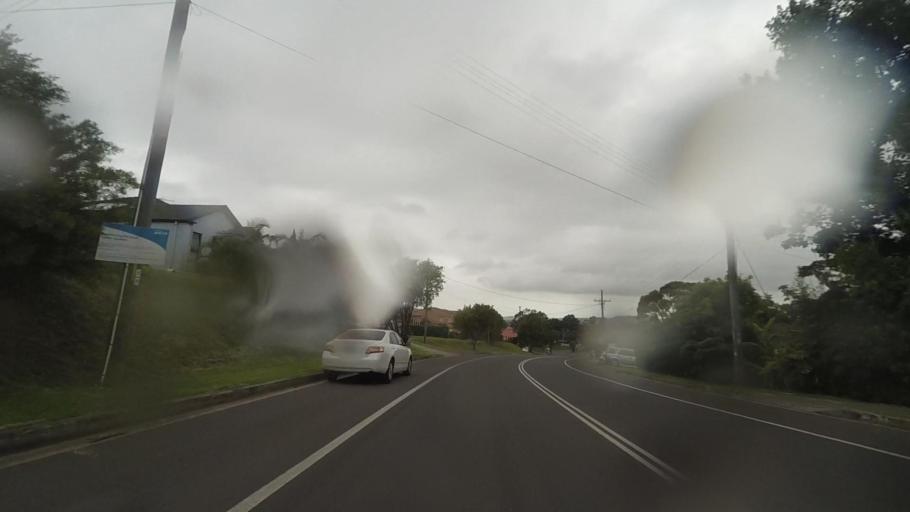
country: AU
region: New South Wales
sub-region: Wollongong
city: Mount Keira
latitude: -34.4164
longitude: 150.8597
